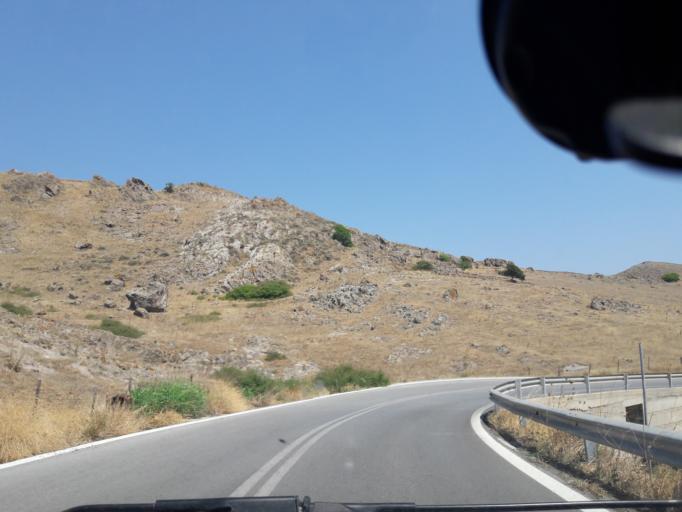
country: GR
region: North Aegean
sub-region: Nomos Lesvou
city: Myrina
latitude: 39.8594
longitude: 25.0826
